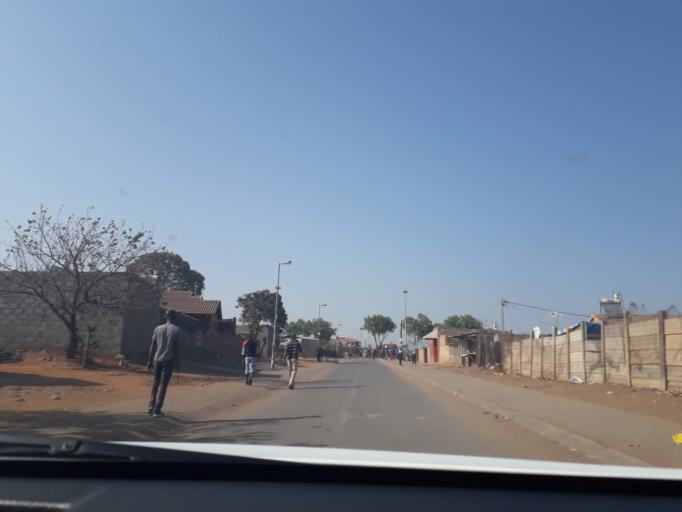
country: ZA
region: Gauteng
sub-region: Ekurhuleni Metropolitan Municipality
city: Tembisa
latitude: -25.9973
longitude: 28.2023
